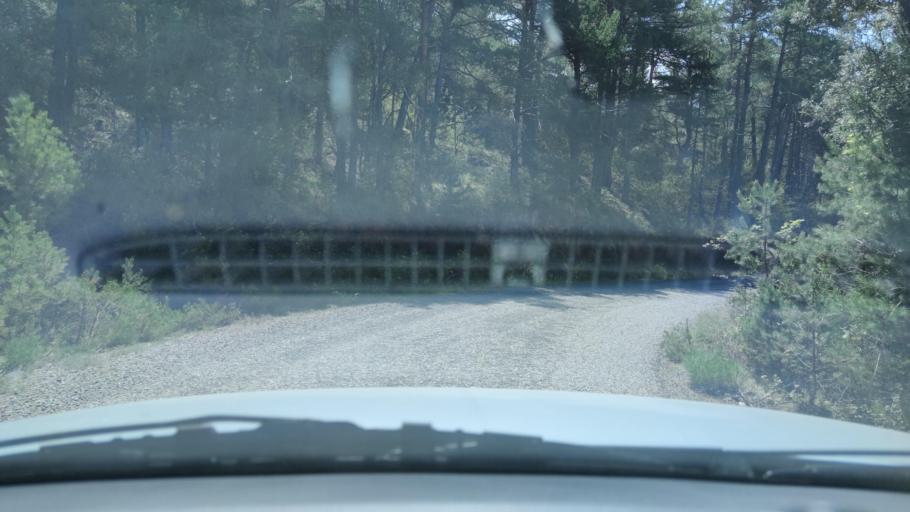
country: ES
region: Catalonia
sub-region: Provincia de Lleida
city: Sort
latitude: 42.3204
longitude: 1.0903
